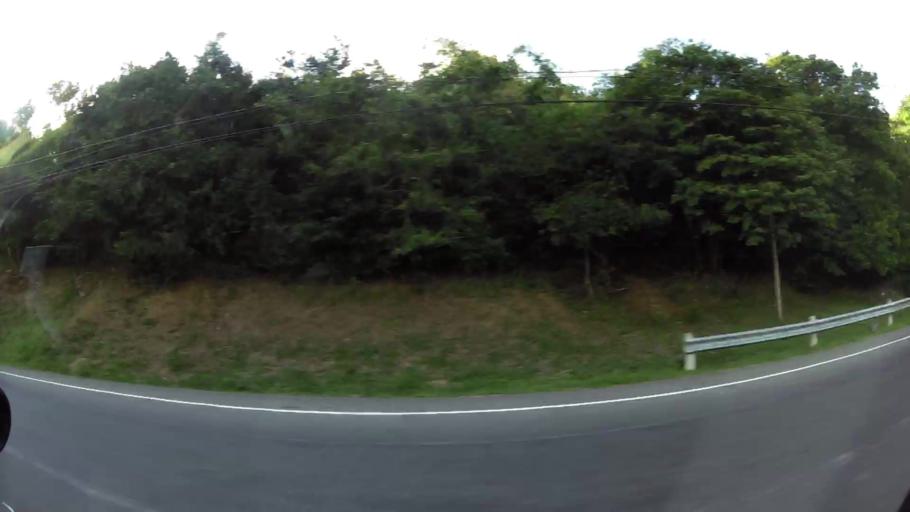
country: TT
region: Tobago
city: Scarborough
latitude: 11.1810
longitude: -60.7044
